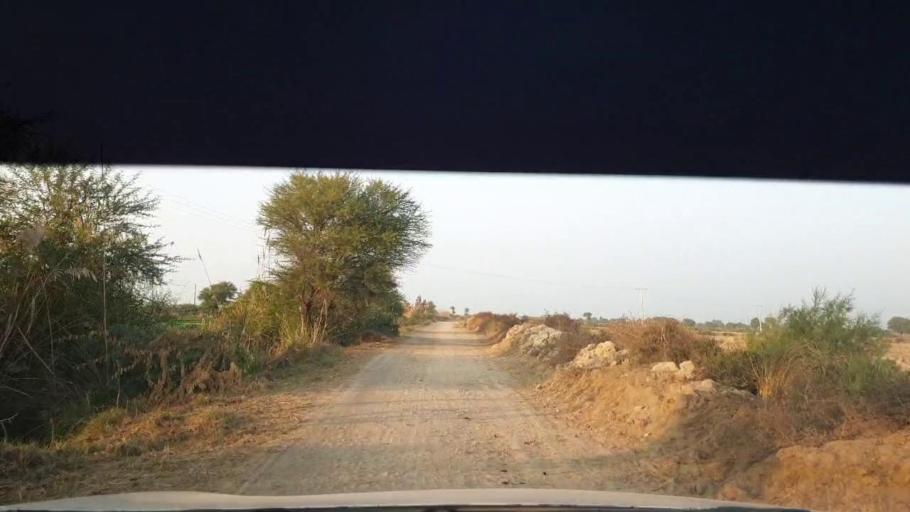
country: PK
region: Sindh
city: Berani
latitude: 25.7552
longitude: 68.9817
